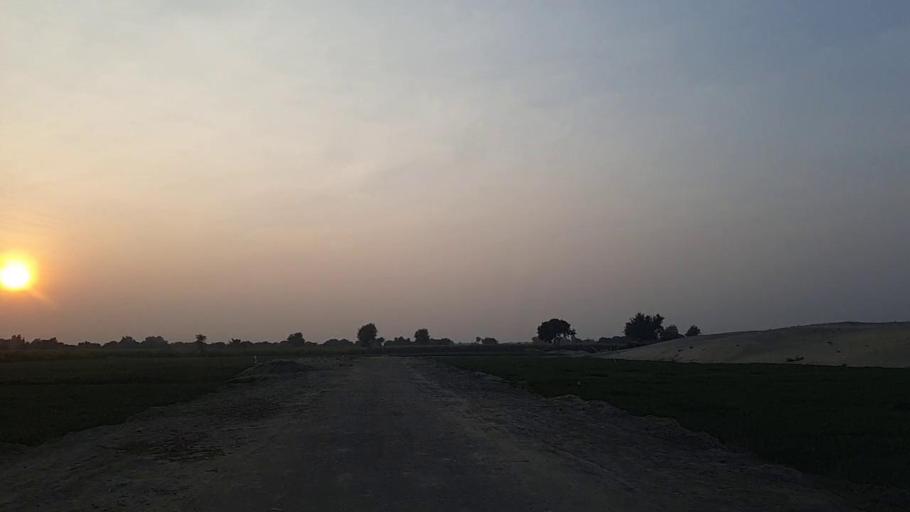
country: PK
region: Sindh
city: Jam Sahib
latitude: 26.4675
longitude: 68.5536
